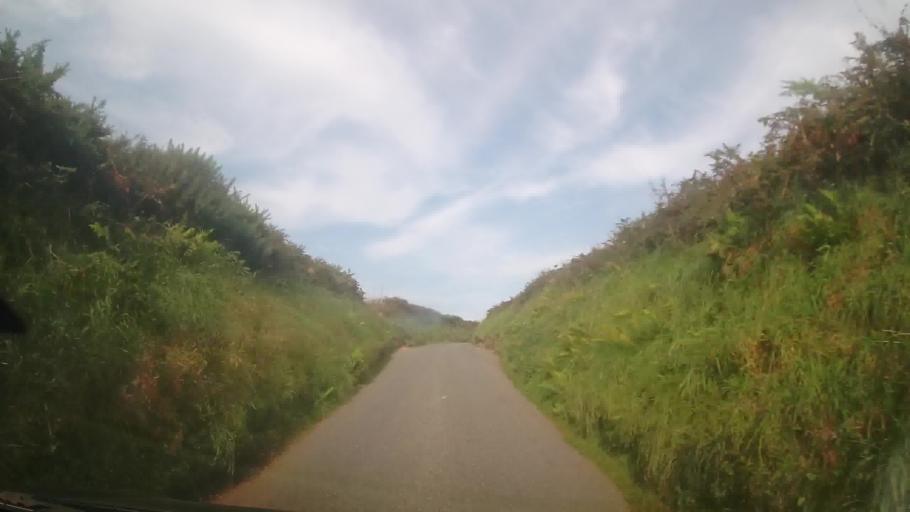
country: GB
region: Wales
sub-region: Pembrokeshire
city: Camrose
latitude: 51.8518
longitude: -5.0652
